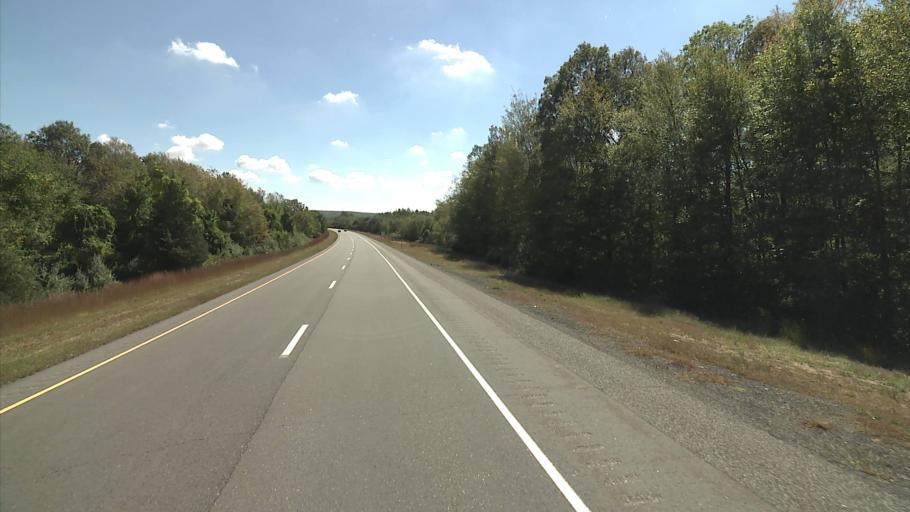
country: US
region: Connecticut
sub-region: New London County
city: Colchester
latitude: 41.4777
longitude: -72.2969
